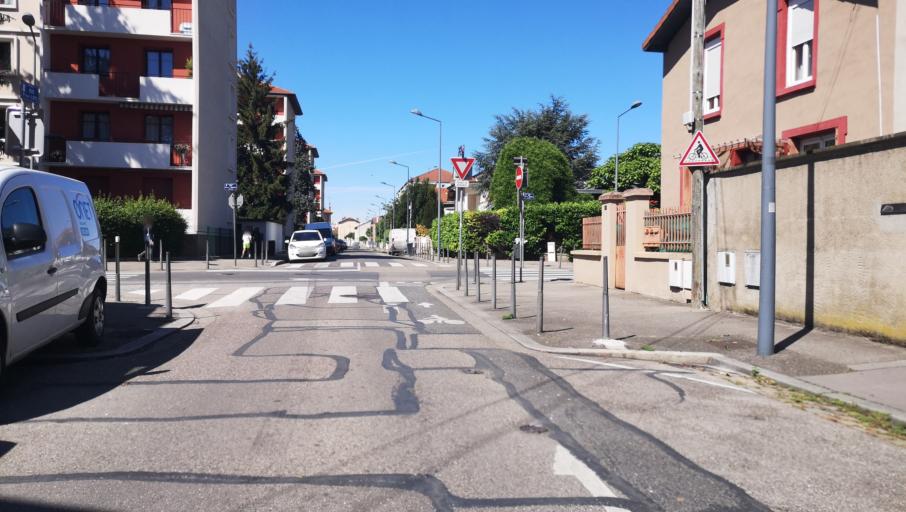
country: FR
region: Rhone-Alpes
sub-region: Departement du Rhone
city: Villeurbanne
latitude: 45.7703
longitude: 4.8876
